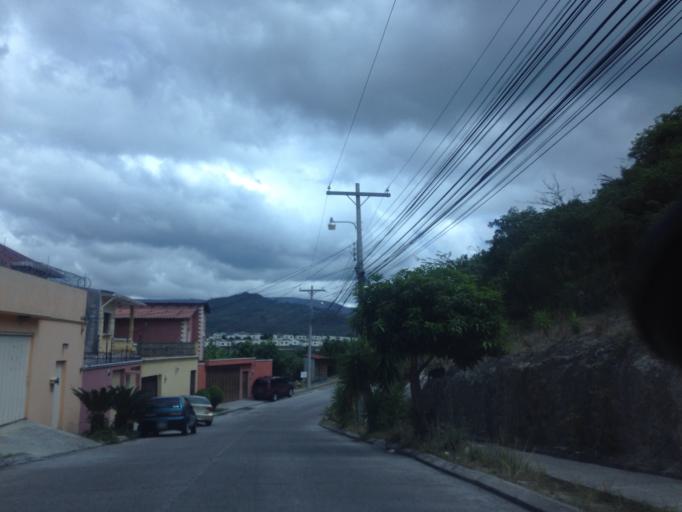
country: HN
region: Francisco Morazan
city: Tegucigalpa
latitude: 14.0535
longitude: -87.2395
